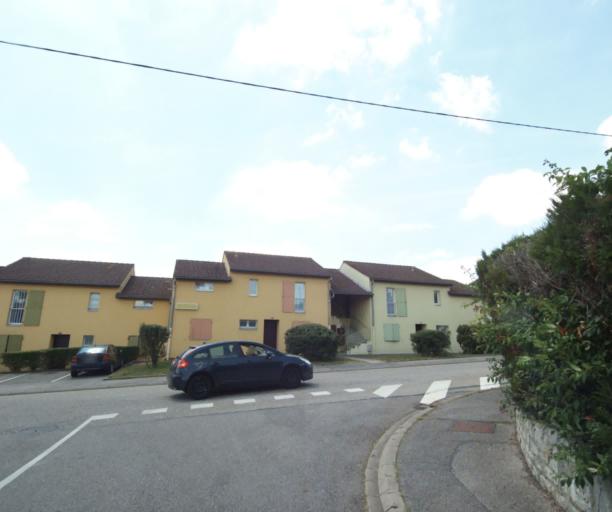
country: FR
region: Lorraine
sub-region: Departement de Meurthe-et-Moselle
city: Luneville
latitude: 48.5979
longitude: 6.4790
